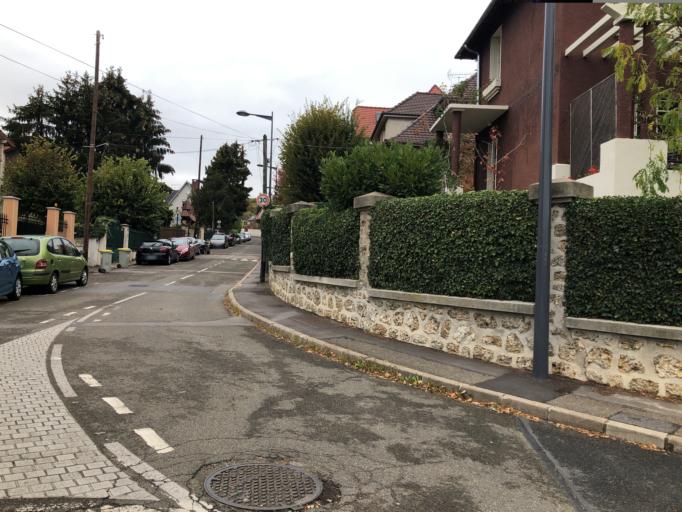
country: FR
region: Ile-de-France
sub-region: Departement des Hauts-de-Seine
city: Chaville
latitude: 48.8075
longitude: 2.1825
